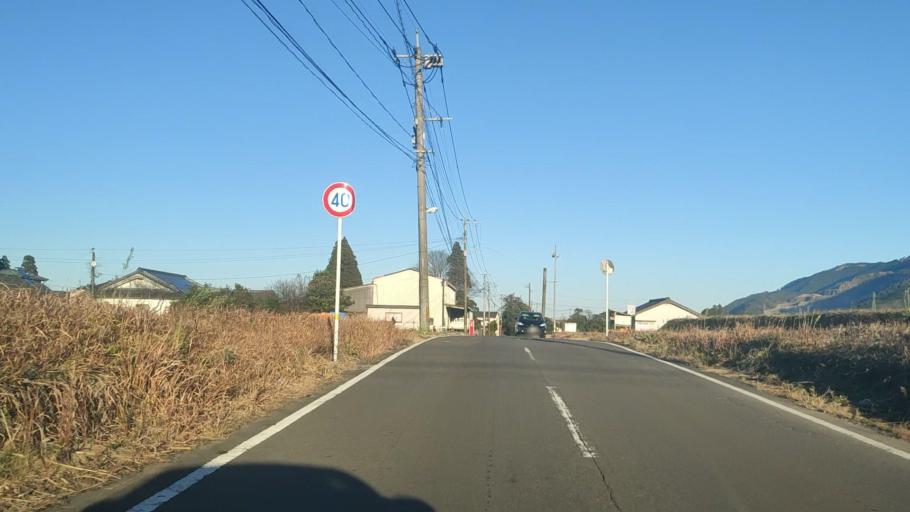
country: JP
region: Miyazaki
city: Miyazaki-shi
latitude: 31.8252
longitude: 131.2987
